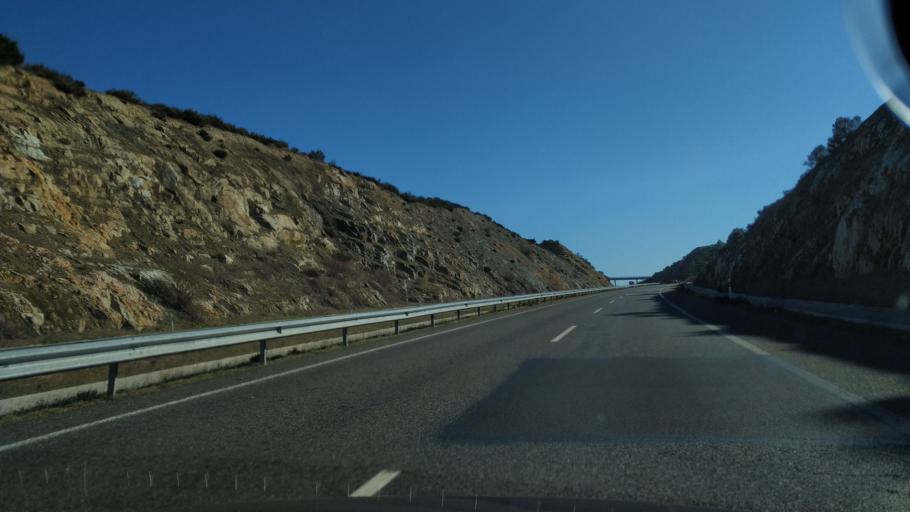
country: ES
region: Galicia
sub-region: Provincia de Ourense
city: Oimbra
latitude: 41.8617
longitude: -7.4267
